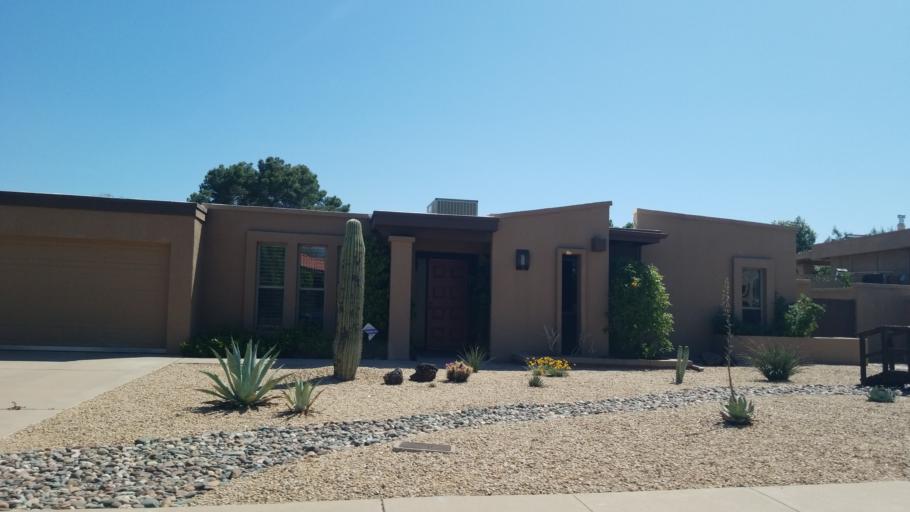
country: US
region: Arizona
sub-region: Maricopa County
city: Paradise Valley
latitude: 33.5810
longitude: -112.0292
